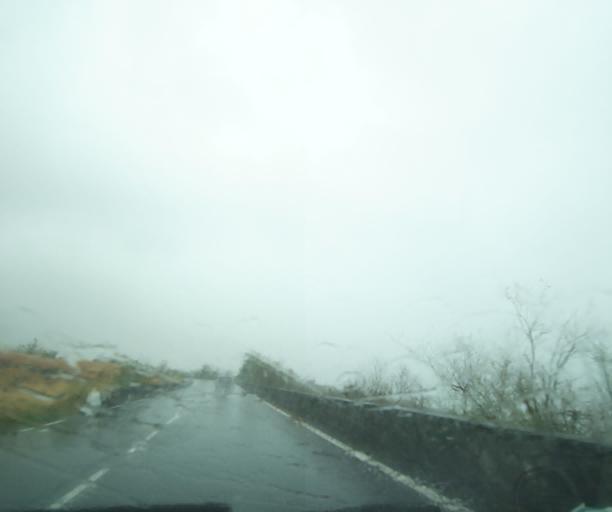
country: RE
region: Reunion
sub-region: Reunion
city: Saint-Paul
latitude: -21.0163
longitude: 55.2668
